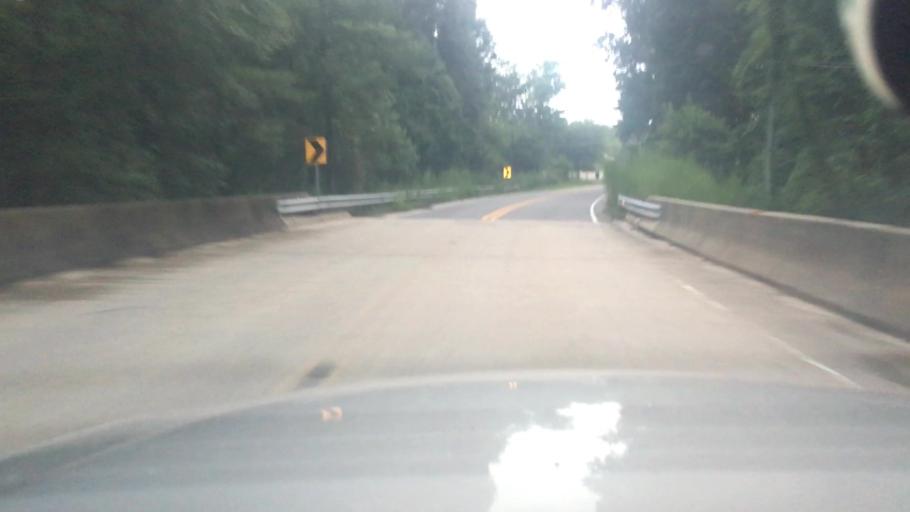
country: US
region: North Carolina
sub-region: Cumberland County
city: Hope Mills
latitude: 34.9665
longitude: -78.9177
